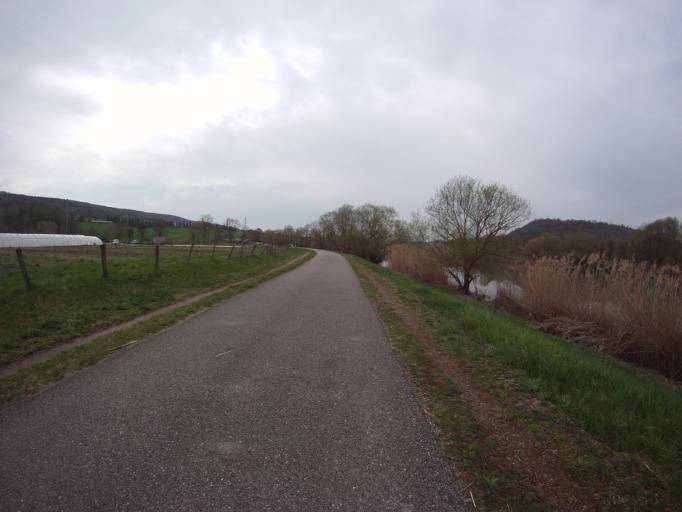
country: FR
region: Lorraine
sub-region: Departement de Meurthe-et-Moselle
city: Champigneulles
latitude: 48.7337
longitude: 6.1723
